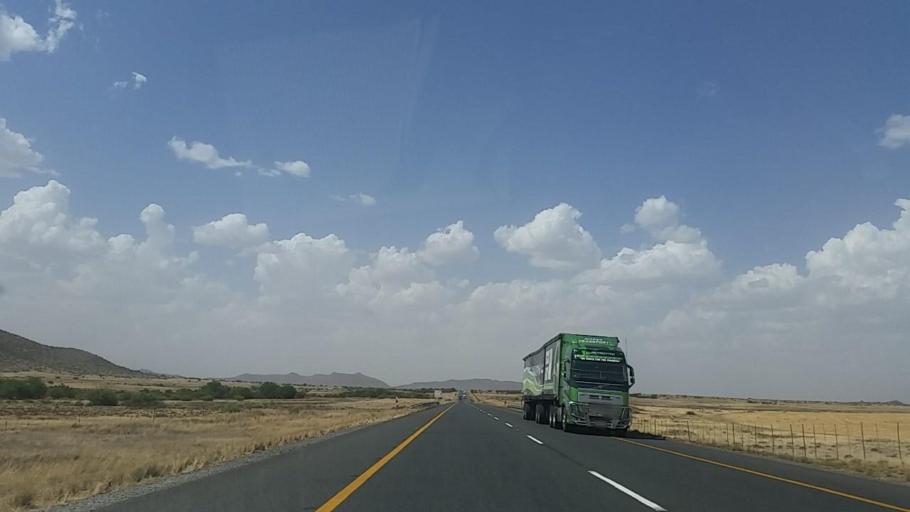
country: ZA
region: Northern Cape
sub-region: Pixley ka Seme District Municipality
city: Colesberg
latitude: -30.5788
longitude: 25.4348
